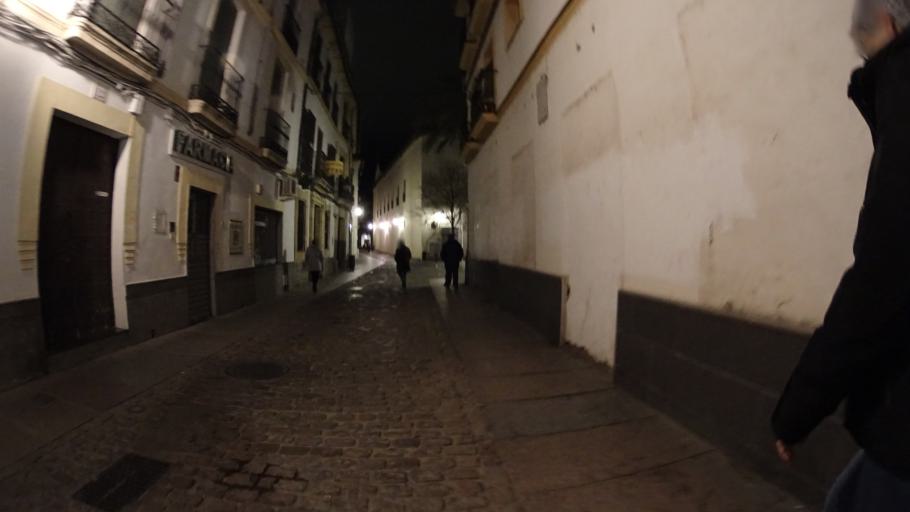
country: ES
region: Andalusia
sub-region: Province of Cordoba
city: Cordoba
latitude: 37.8826
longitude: -4.7748
